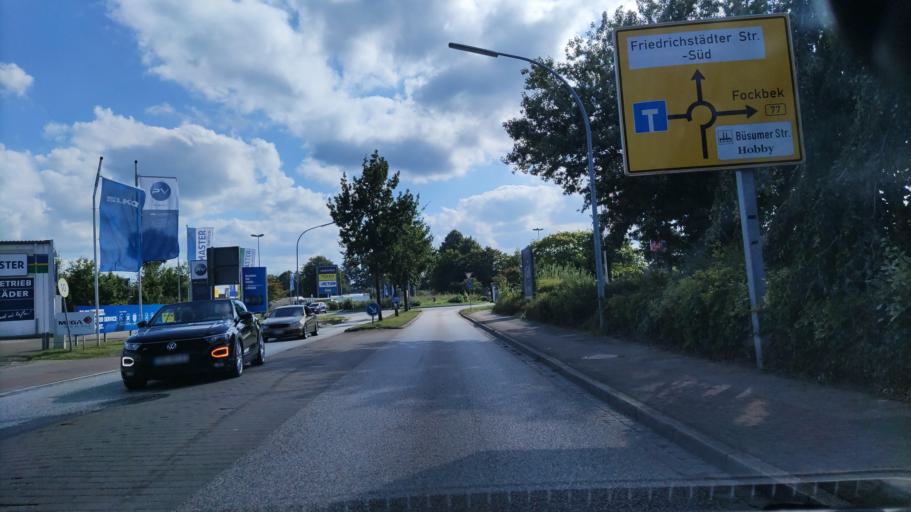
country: DE
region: Schleswig-Holstein
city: Fockbek
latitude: 54.3189
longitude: 9.6266
